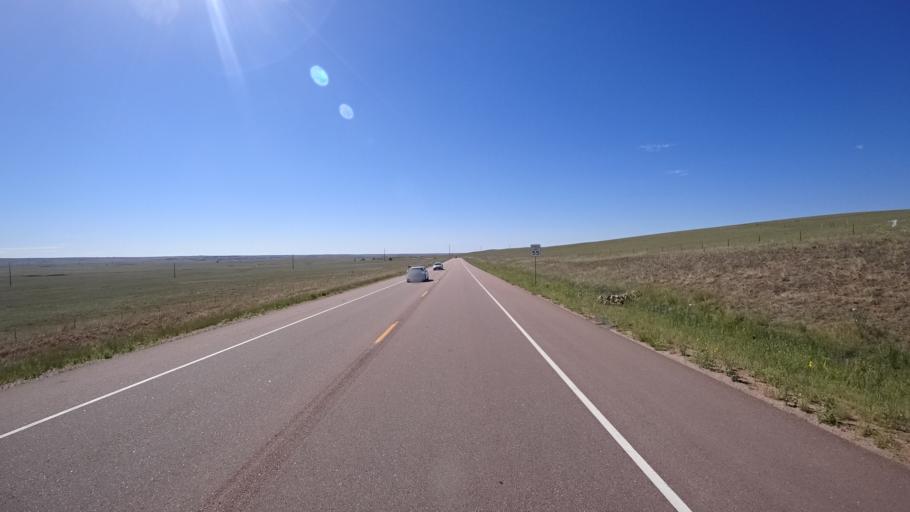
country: US
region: Colorado
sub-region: El Paso County
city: Cimarron Hills
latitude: 38.8124
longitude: -104.6727
